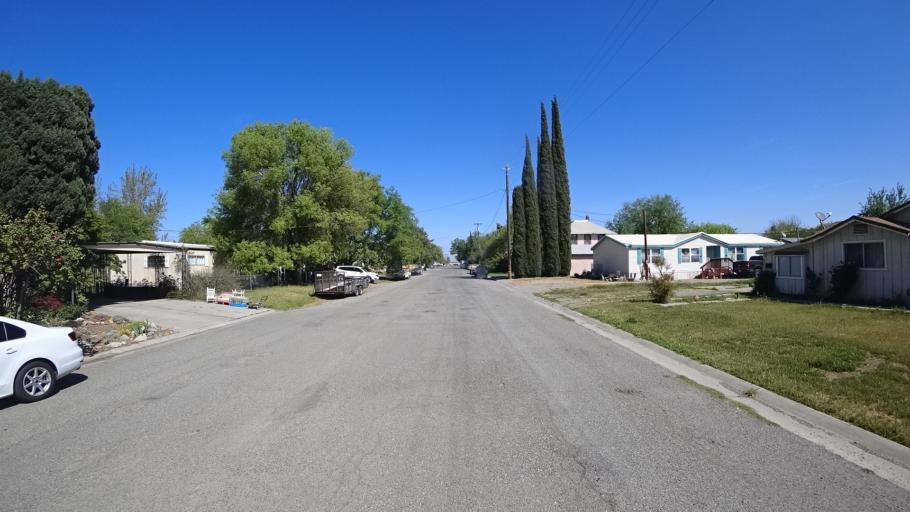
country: US
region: California
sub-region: Glenn County
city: Willows
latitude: 39.5274
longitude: -122.1909
